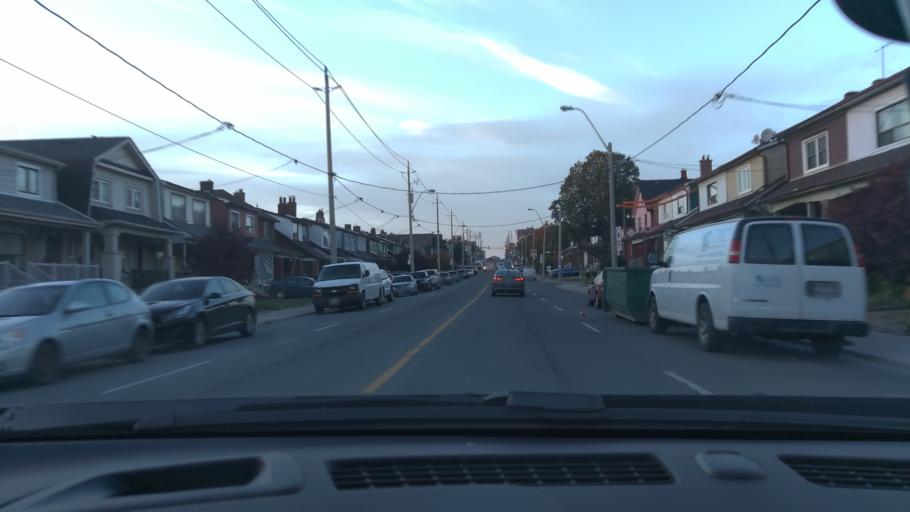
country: CA
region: Ontario
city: Toronto
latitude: 43.6827
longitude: -79.4449
